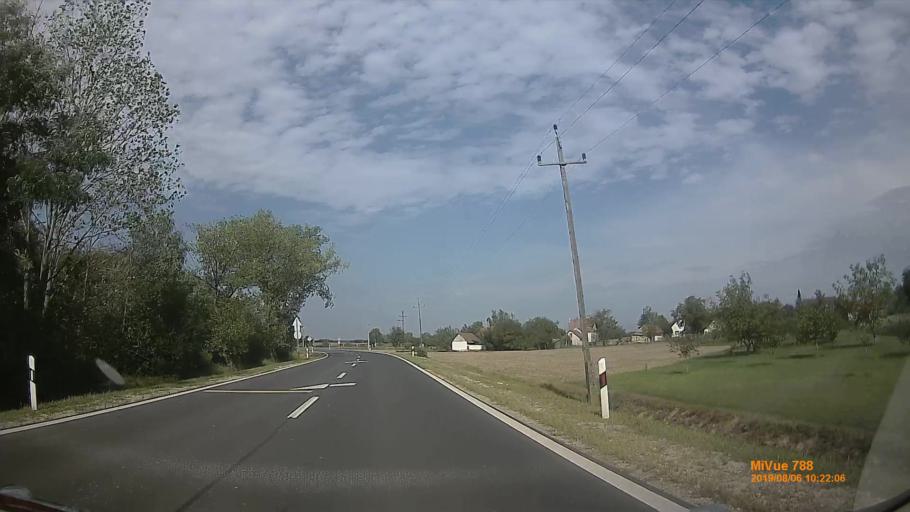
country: HU
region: Vas
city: Vasvar
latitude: 47.0693
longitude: 16.7379
